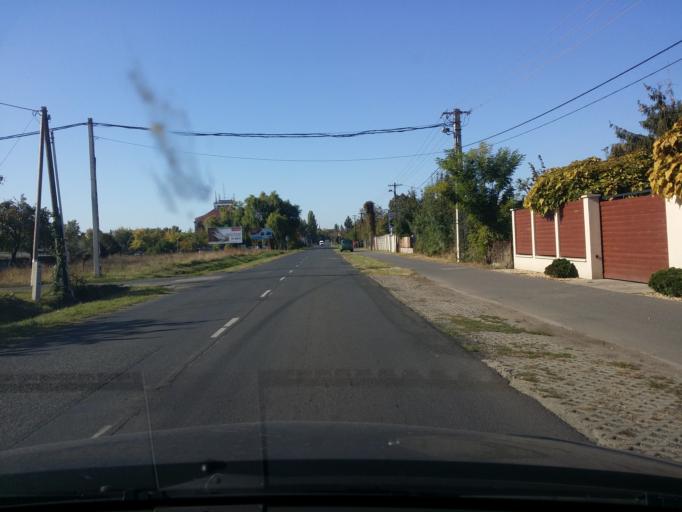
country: HU
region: Bekes
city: Bekescsaba
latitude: 46.6868
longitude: 21.1159
